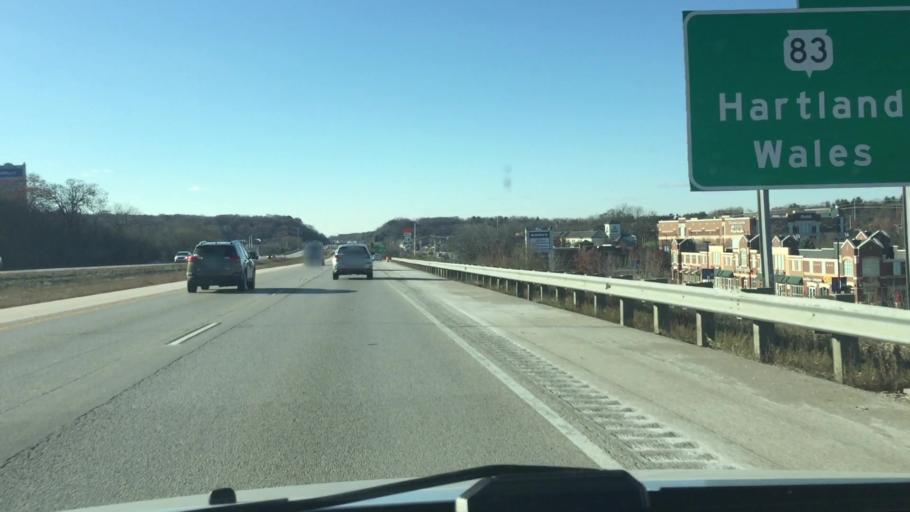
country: US
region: Wisconsin
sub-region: Waukesha County
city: Delafield
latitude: 43.0508
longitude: -88.3655
